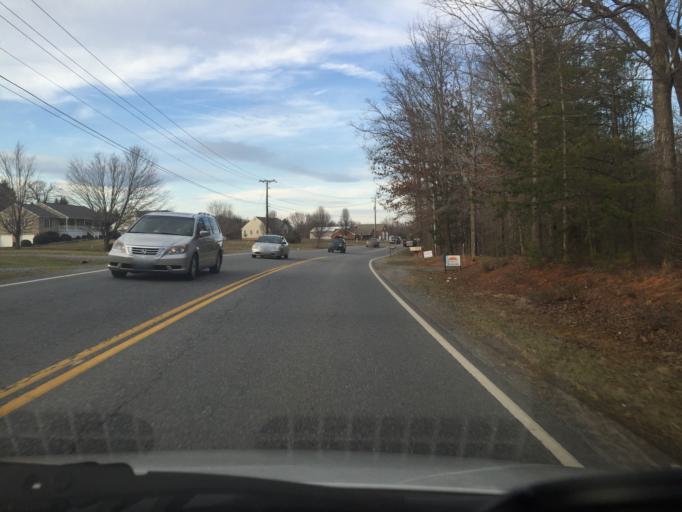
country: US
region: Virginia
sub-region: Bedford County
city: Forest
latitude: 37.3405
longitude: -79.2852
